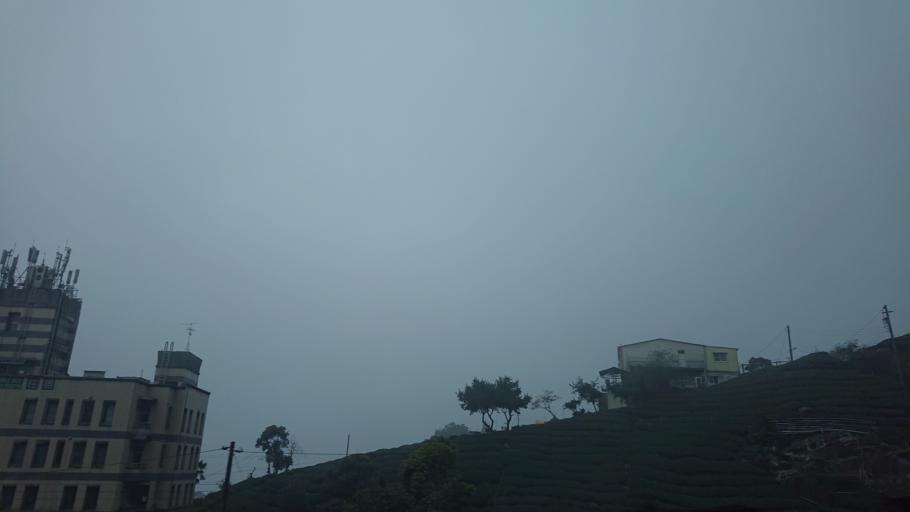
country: TW
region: Taiwan
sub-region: Chiayi
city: Jiayi Shi
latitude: 23.4740
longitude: 120.6984
